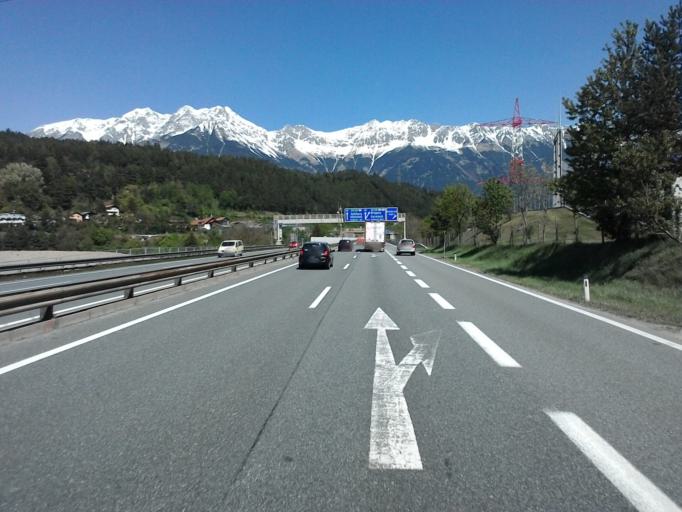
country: AT
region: Tyrol
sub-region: Politischer Bezirk Innsbruck Land
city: Mutters
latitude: 47.2357
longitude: 11.3918
